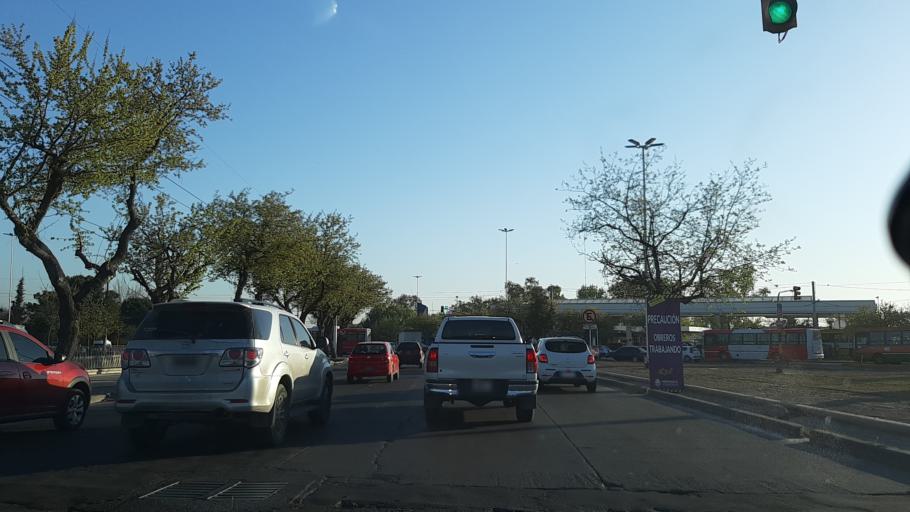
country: AR
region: Mendoza
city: Mendoza
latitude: -32.8935
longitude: -68.8310
